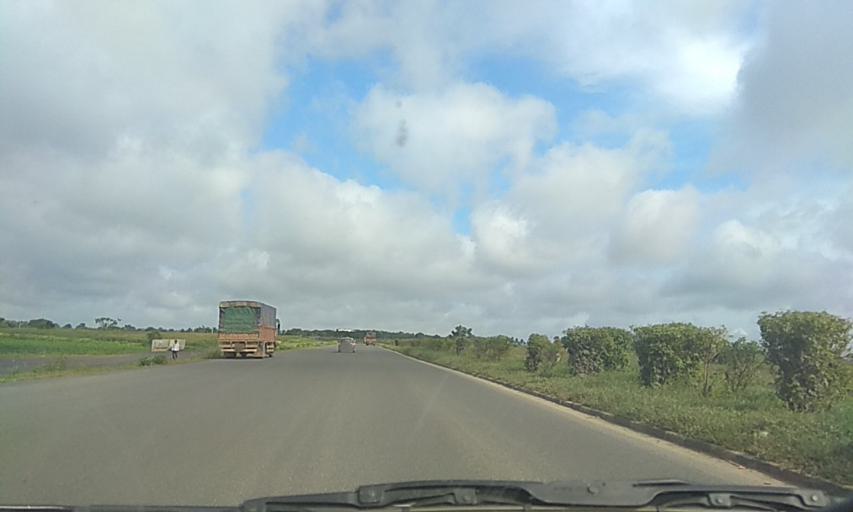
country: IN
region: Karnataka
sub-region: Haveri
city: Shiggaon
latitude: 15.0013
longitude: 75.2066
